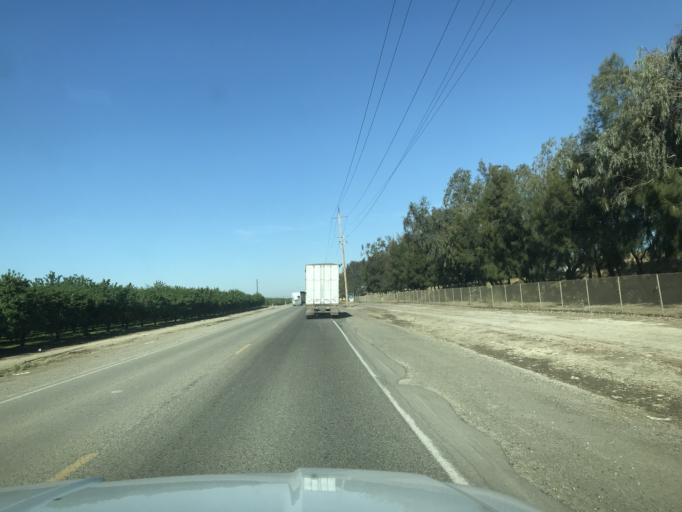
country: US
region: California
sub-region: Fresno County
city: San Joaquin
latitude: 36.6618
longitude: -120.1312
